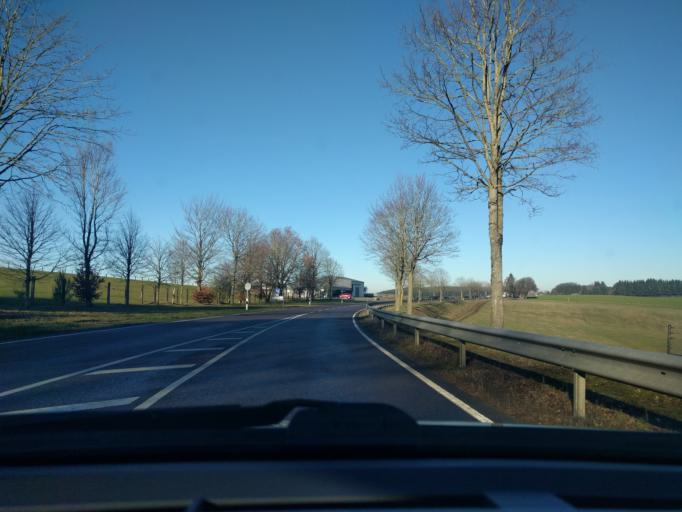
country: LU
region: Diekirch
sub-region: Canton de Clervaux
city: Troisvierges
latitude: 50.1623
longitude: 6.0268
